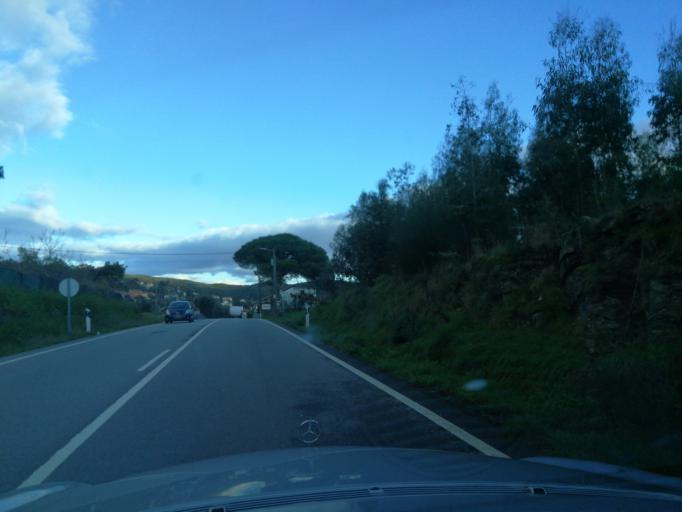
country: PT
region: Braga
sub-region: Barcelos
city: Vila Frescainha
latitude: 41.5728
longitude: -8.7006
